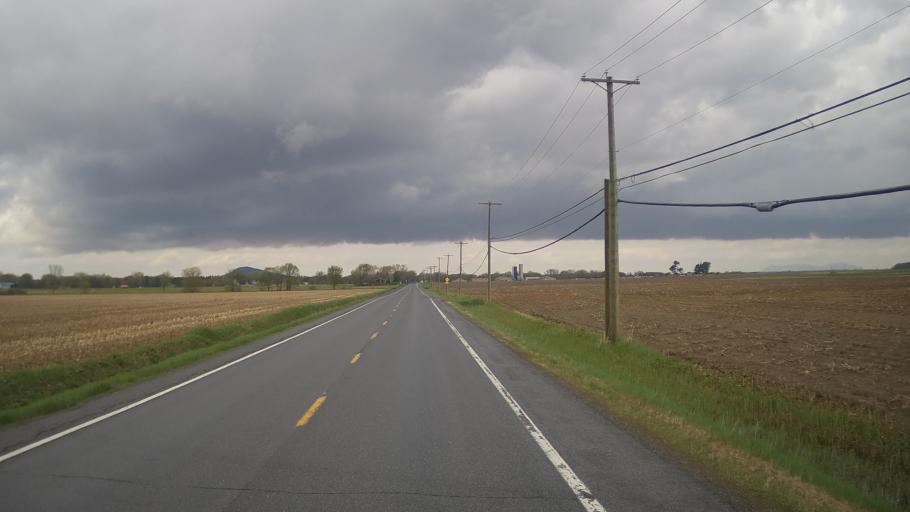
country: CA
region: Quebec
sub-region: Monteregie
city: Farnham
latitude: 45.3125
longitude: -73.0496
